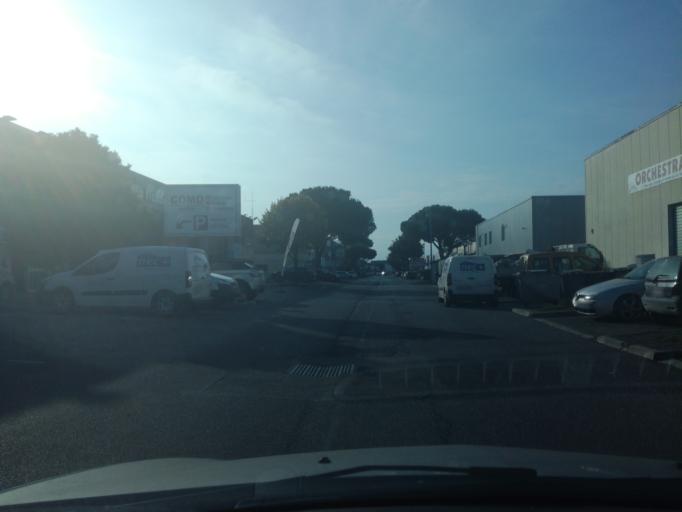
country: FR
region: Provence-Alpes-Cote d'Azur
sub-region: Departement des Alpes-Maritimes
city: Mandelieu-la-Napoule
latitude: 43.5555
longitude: 6.9554
